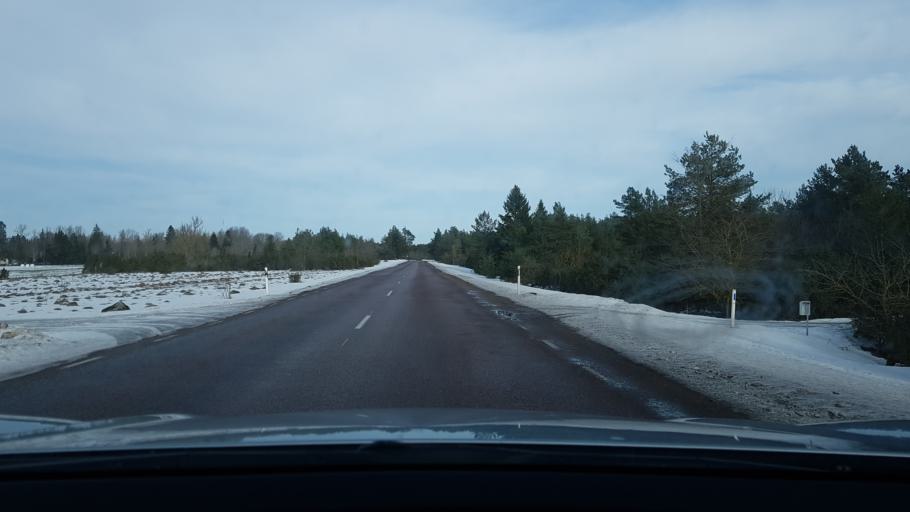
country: EE
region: Saare
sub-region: Kuressaare linn
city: Kuressaare
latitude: 58.3353
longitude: 22.5678
